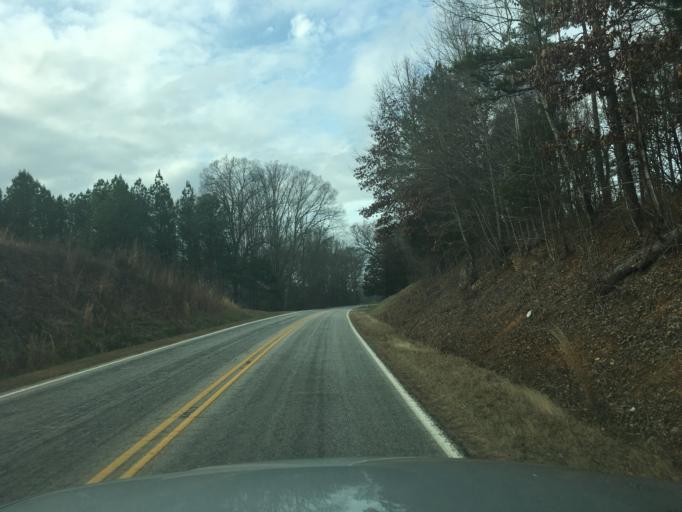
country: US
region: South Carolina
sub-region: Abbeville County
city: Due West
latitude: 34.2909
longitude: -82.4465
